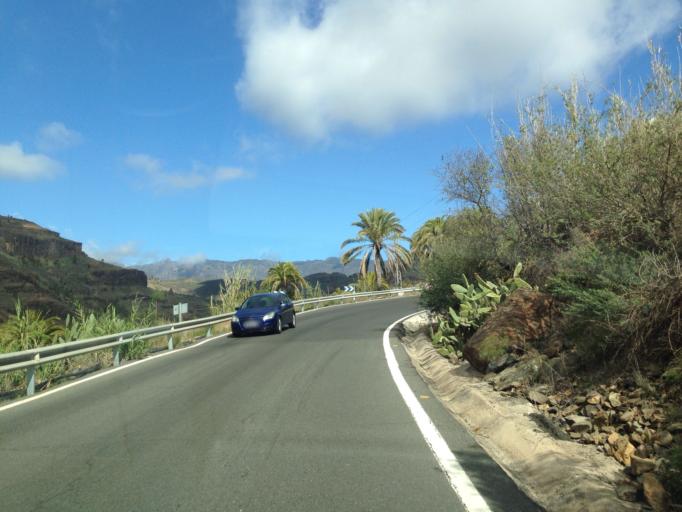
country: ES
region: Canary Islands
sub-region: Provincia de Las Palmas
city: Santa Lucia
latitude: 27.8800
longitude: -15.5662
